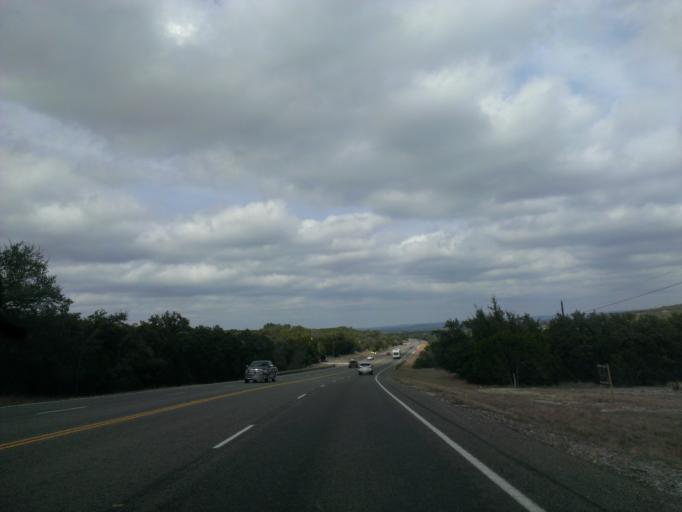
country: US
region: Texas
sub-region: Travis County
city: Briarcliff
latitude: 30.4437
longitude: -98.1476
